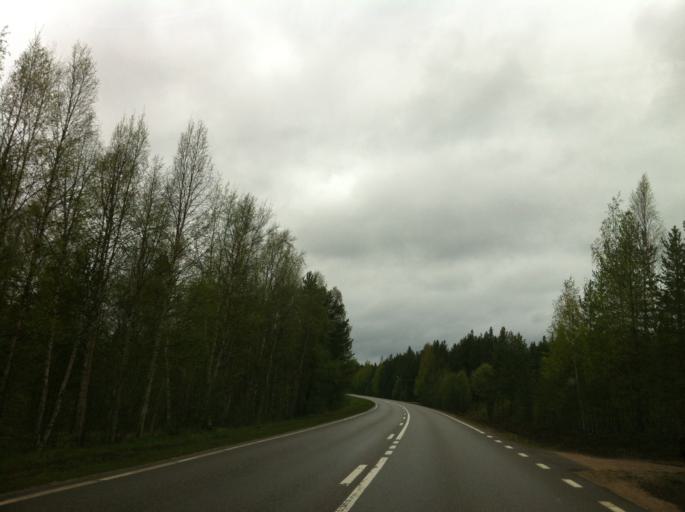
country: SE
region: Jaemtland
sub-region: Harjedalens Kommun
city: Sveg
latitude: 62.1334
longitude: 14.0530
